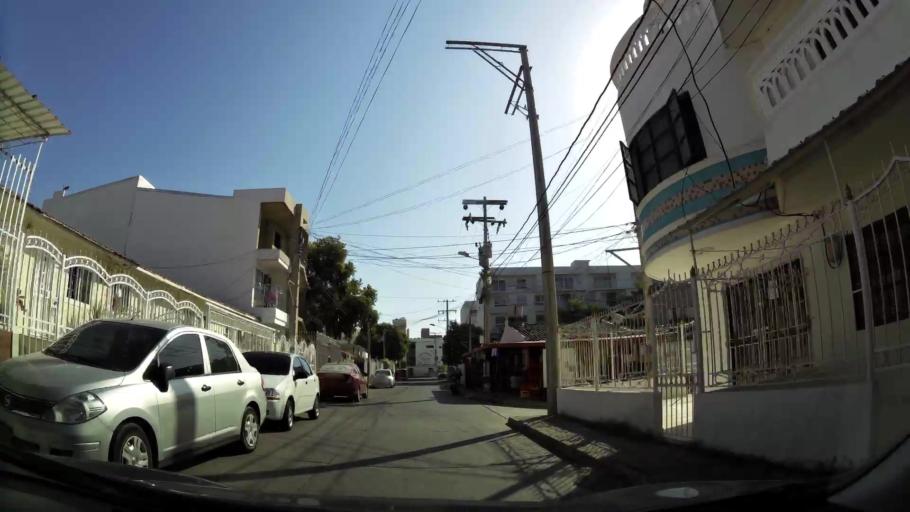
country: CO
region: Bolivar
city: Cartagena
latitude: 10.3909
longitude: -75.4987
